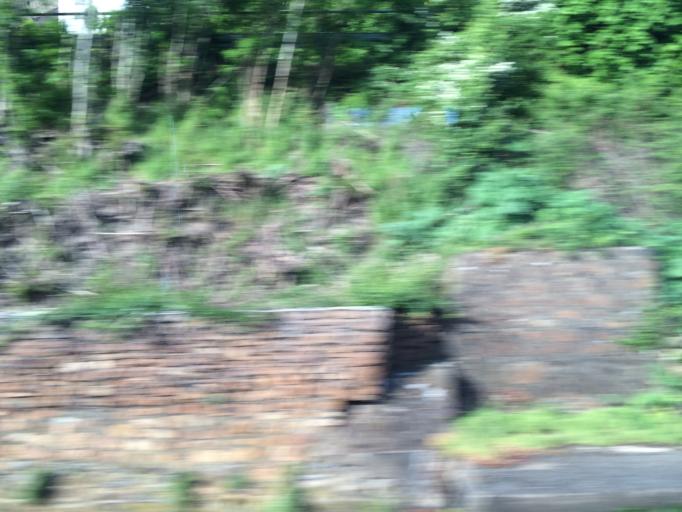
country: DE
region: Rheinland-Pfalz
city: Oberdiebach
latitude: 50.0468
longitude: 7.7931
